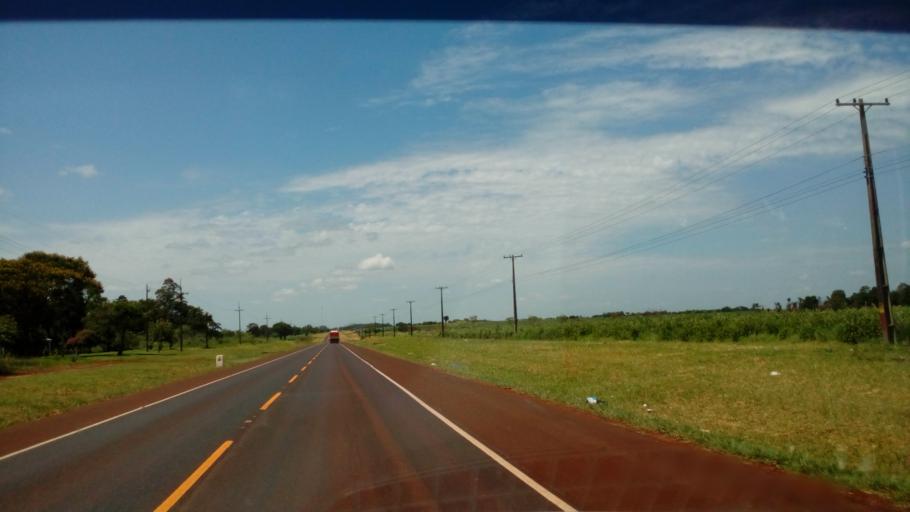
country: PY
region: Alto Parana
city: Colonia Yguazu
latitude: -25.5374
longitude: -54.9022
